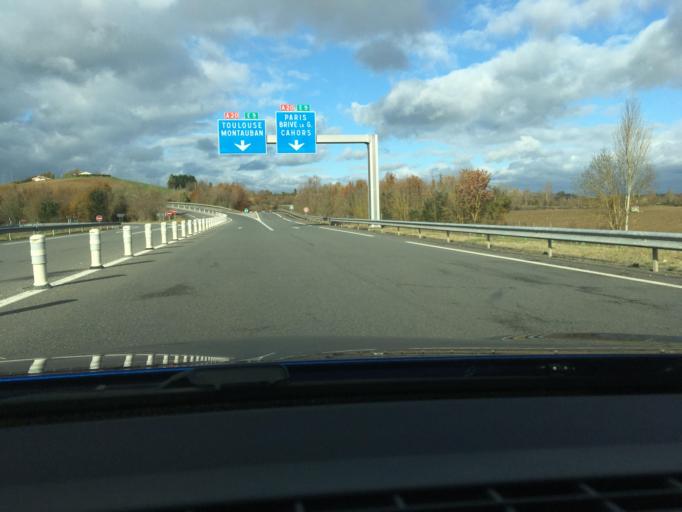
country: FR
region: Midi-Pyrenees
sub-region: Departement du Tarn-et-Garonne
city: Caussade
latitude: 44.1511
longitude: 1.5154
